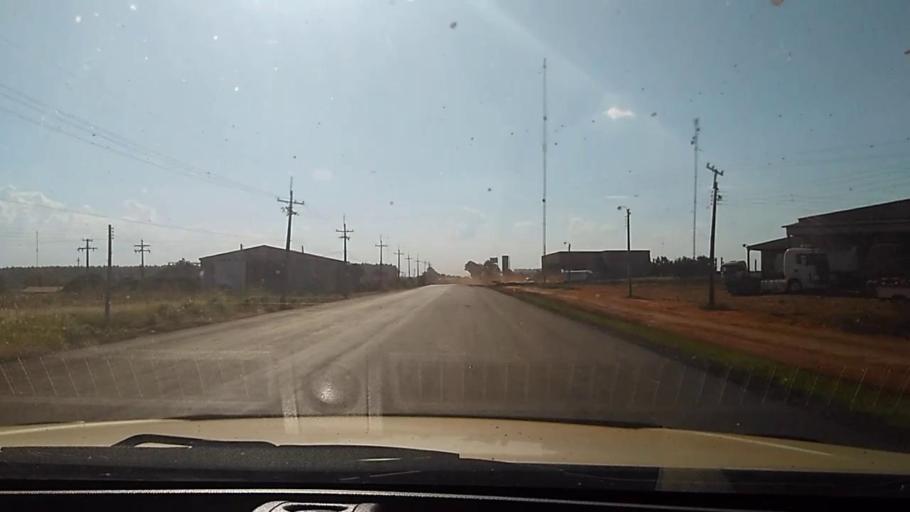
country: PY
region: Alto Parana
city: Naranjal
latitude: -25.9000
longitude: -55.4548
